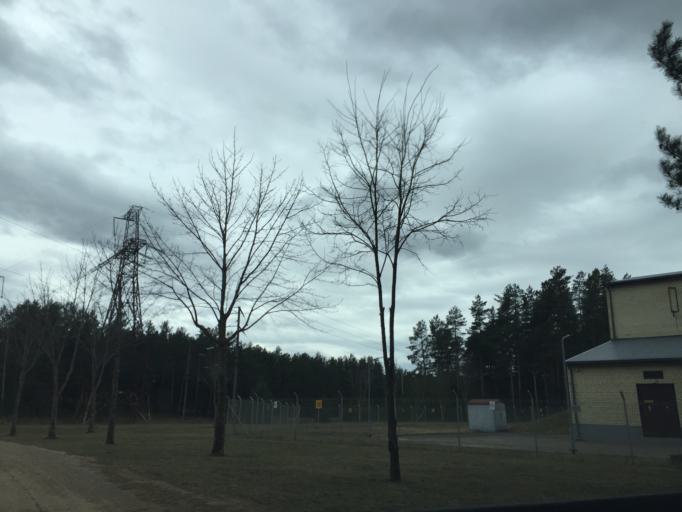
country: LV
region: Daugavpils
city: Daugavpils
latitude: 55.9106
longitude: 26.5406
